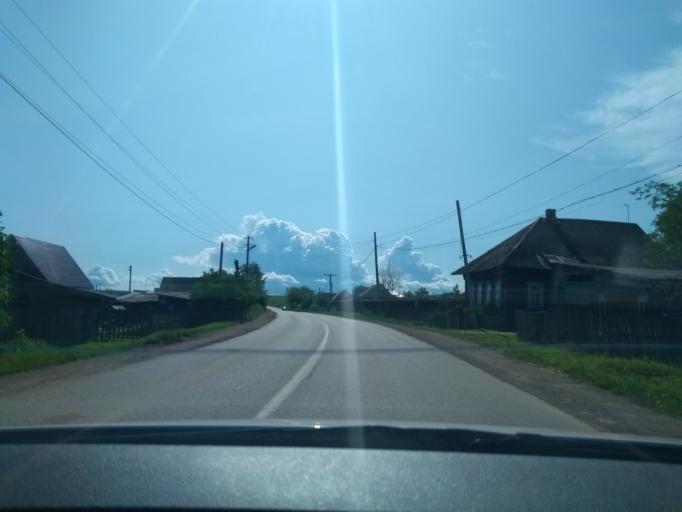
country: RU
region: Perm
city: Lobanovo
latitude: 57.8578
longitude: 56.3064
